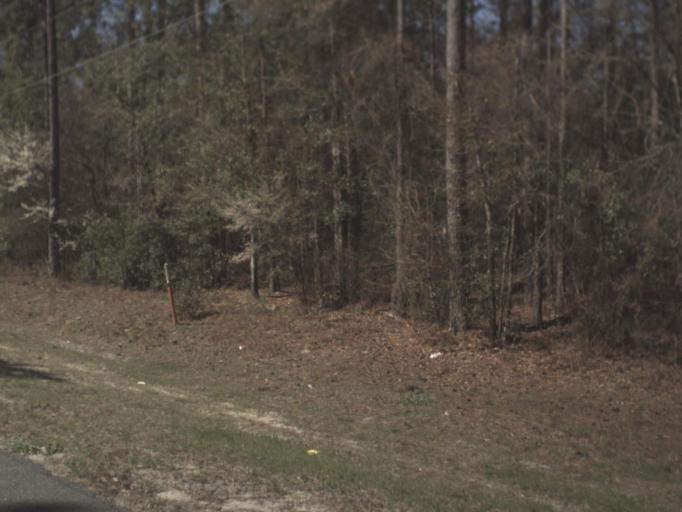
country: US
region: Florida
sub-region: Leon County
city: Woodville
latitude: 30.3072
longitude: -84.3446
